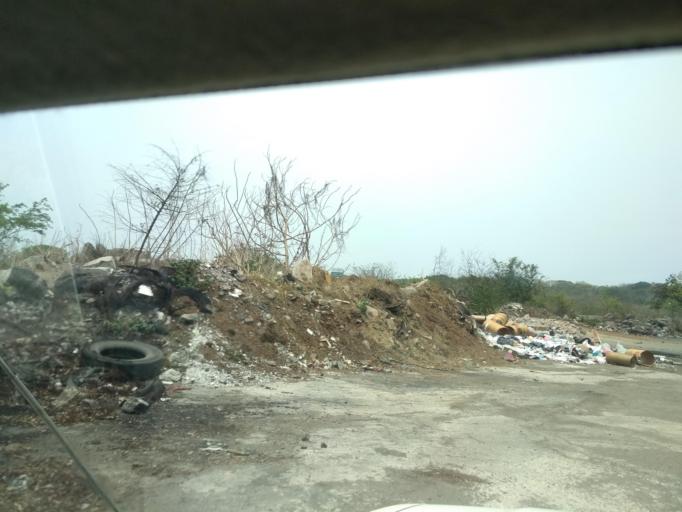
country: MX
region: Veracruz
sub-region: Veracruz
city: Oasis
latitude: 19.1920
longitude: -96.2449
